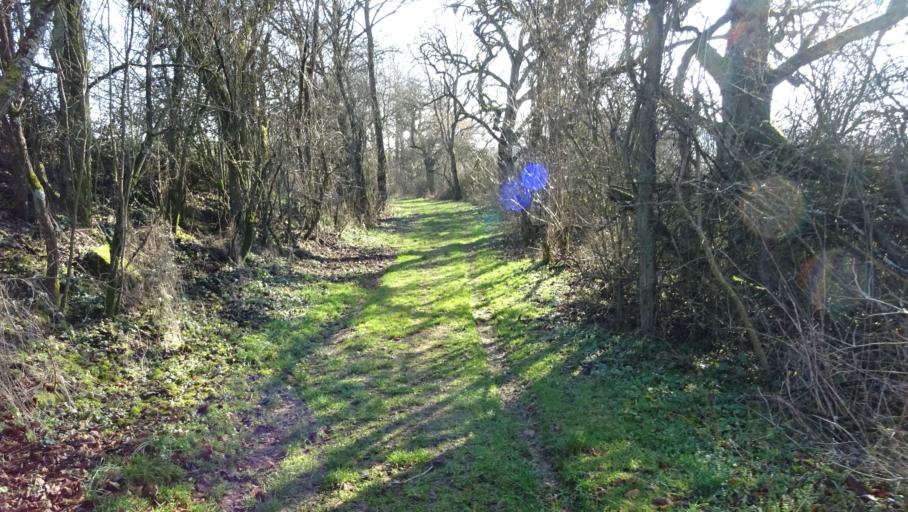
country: DE
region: Baden-Wuerttemberg
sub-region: Karlsruhe Region
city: Mosbach
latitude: 49.3663
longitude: 9.1966
